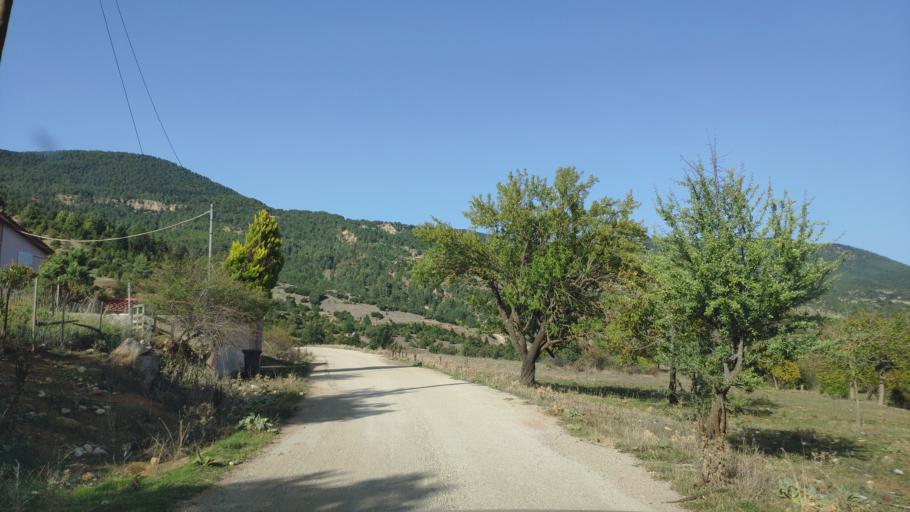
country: GR
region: West Greece
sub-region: Nomos Achaias
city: Aiyira
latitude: 37.9915
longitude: 22.3541
